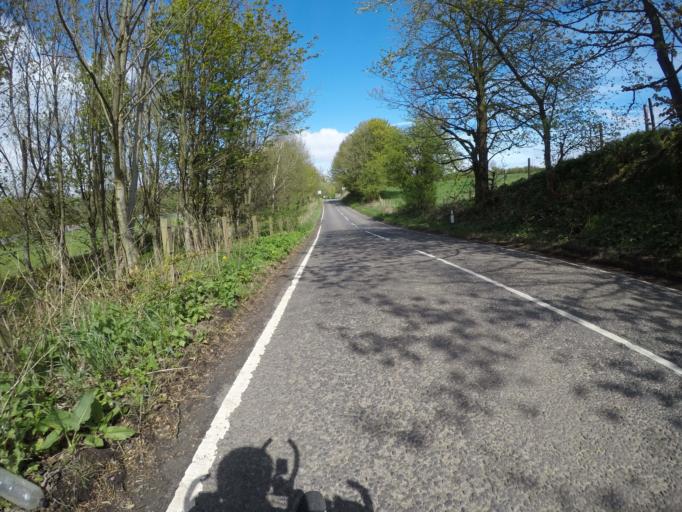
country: GB
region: Scotland
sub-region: East Ayrshire
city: Stewarton
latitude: 55.6749
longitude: -4.5222
